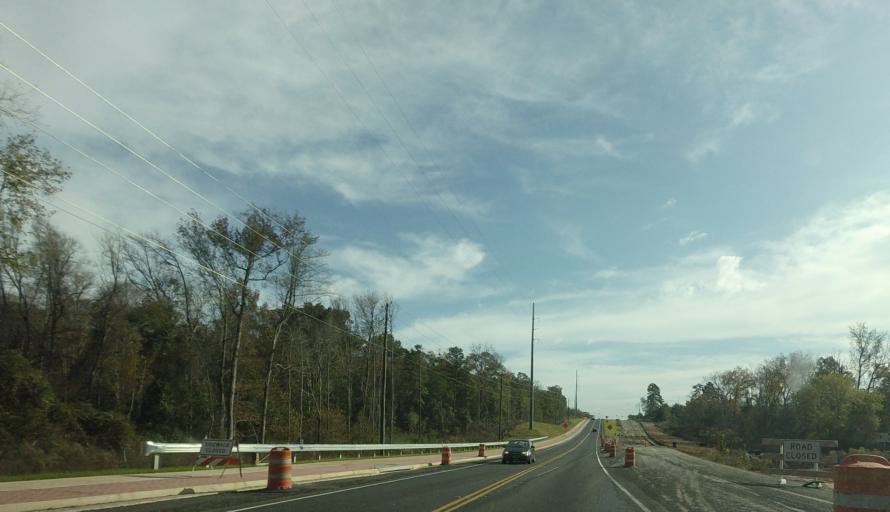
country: US
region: Georgia
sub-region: Houston County
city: Perry
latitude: 32.5465
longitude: -83.7249
